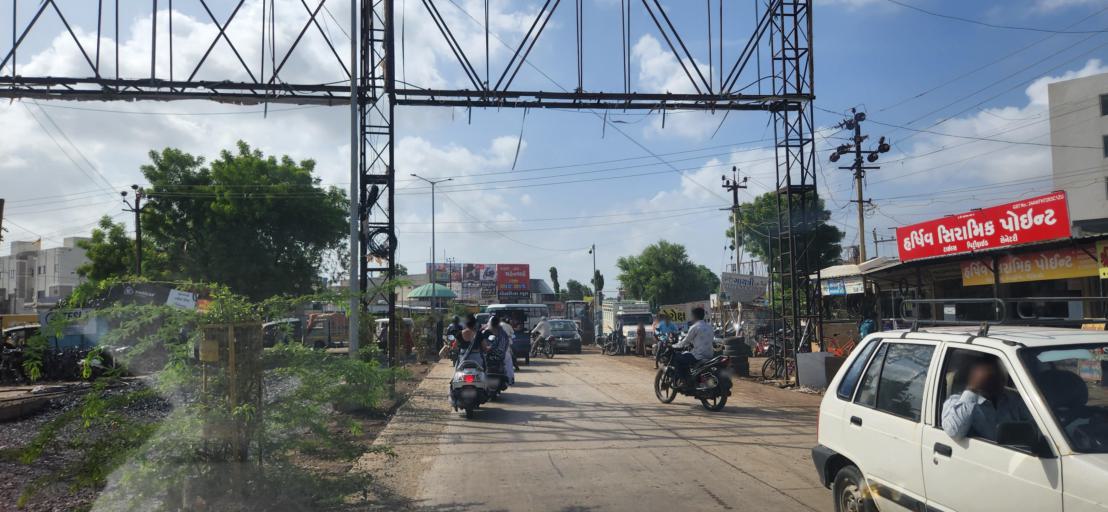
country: IN
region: Gujarat
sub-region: Bhavnagar
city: Bhavnagar
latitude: 21.7334
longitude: 72.1534
